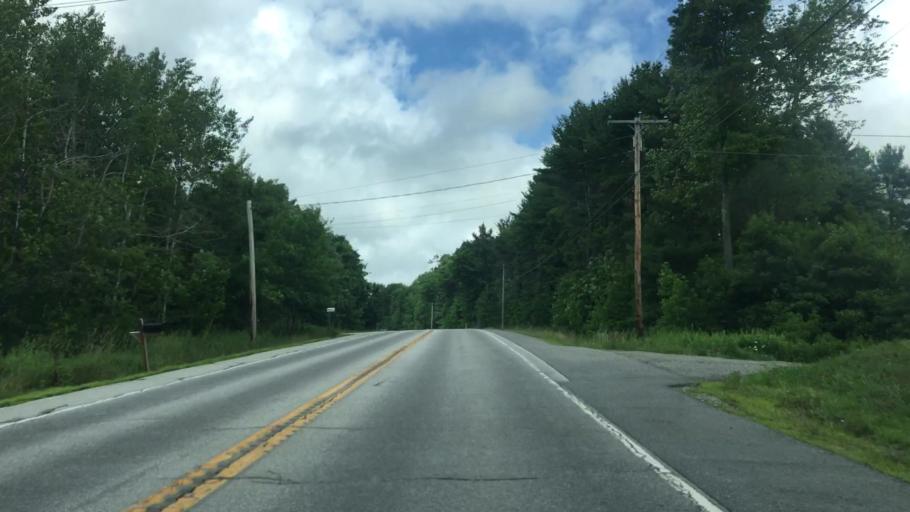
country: US
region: Maine
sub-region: Kennebec County
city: Farmingdale
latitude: 44.2628
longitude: -69.7644
